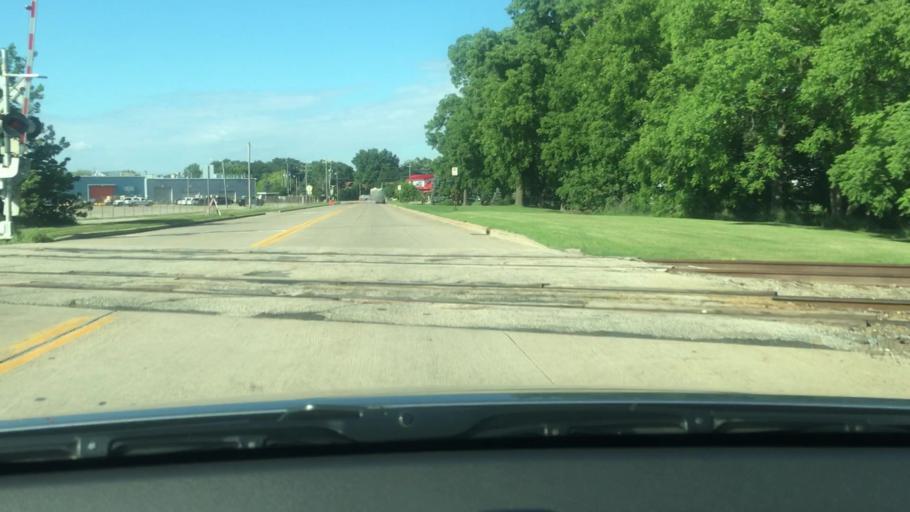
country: US
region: Wisconsin
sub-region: Winnebago County
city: Oshkosh
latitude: 43.9899
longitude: -88.5448
